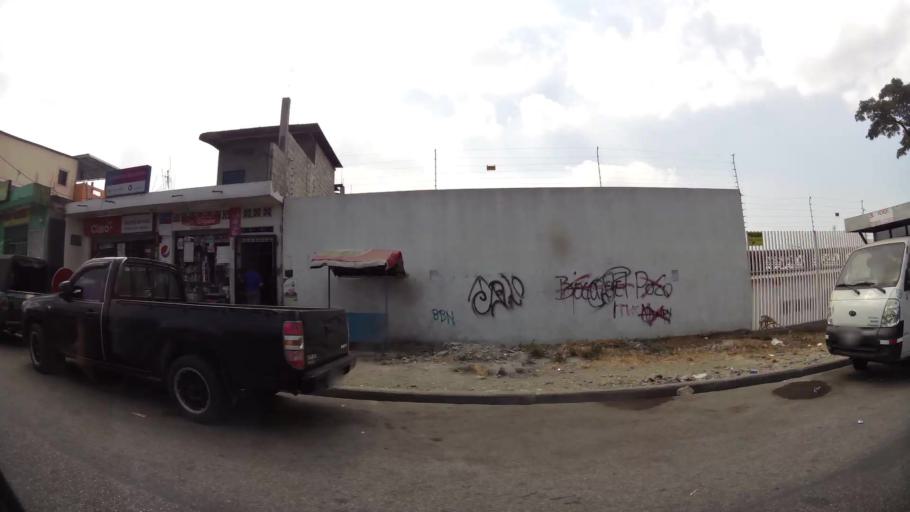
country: EC
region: Guayas
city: Santa Lucia
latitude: -2.1288
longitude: -79.9440
